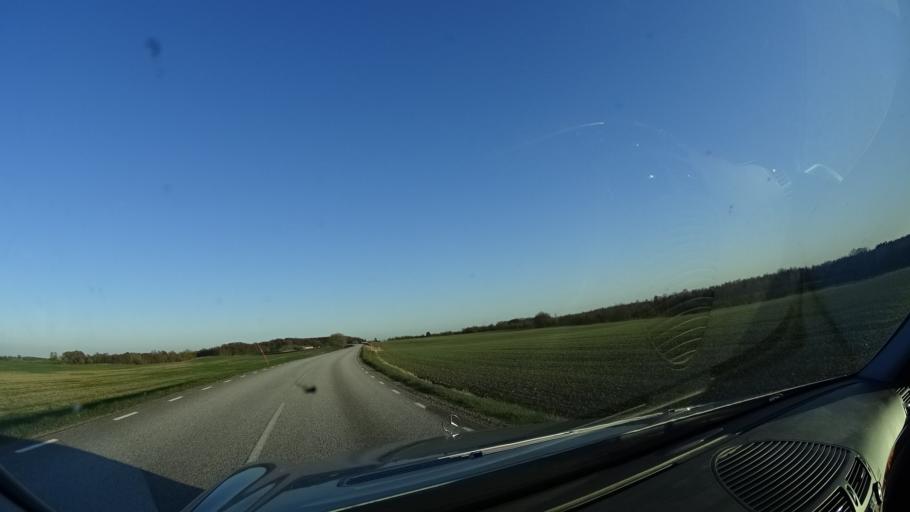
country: SE
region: Skane
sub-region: Klippans Kommun
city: Ljungbyhed
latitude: 55.9755
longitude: 13.2023
